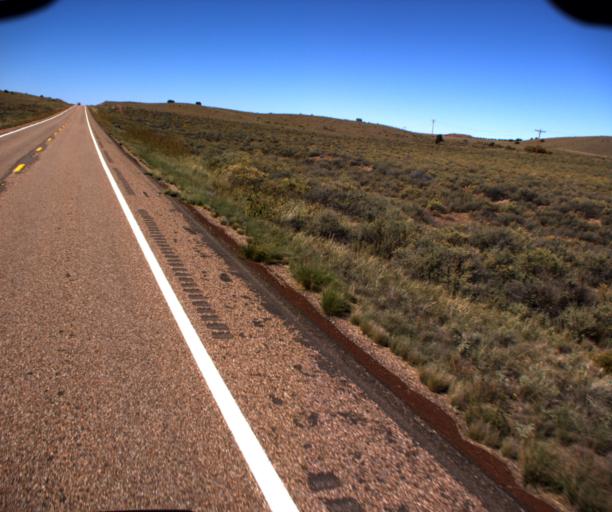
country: US
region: Arizona
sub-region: Apache County
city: Saint Johns
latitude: 34.5858
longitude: -109.5798
